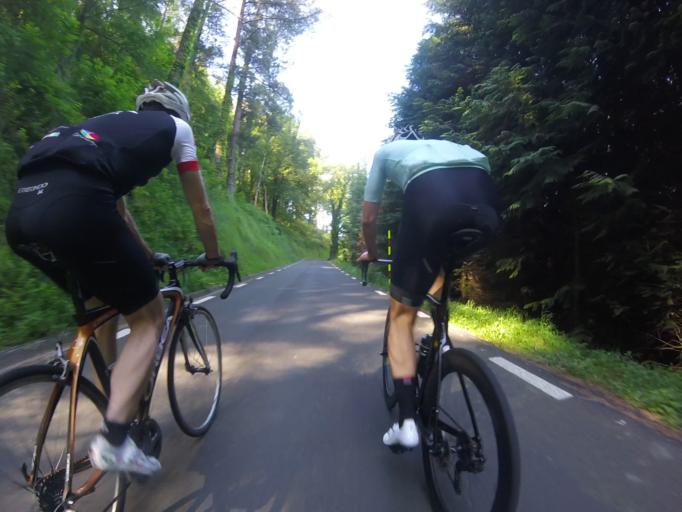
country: ES
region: Basque Country
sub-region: Provincia de Guipuzcoa
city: Beizama
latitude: 43.1371
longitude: -2.2232
